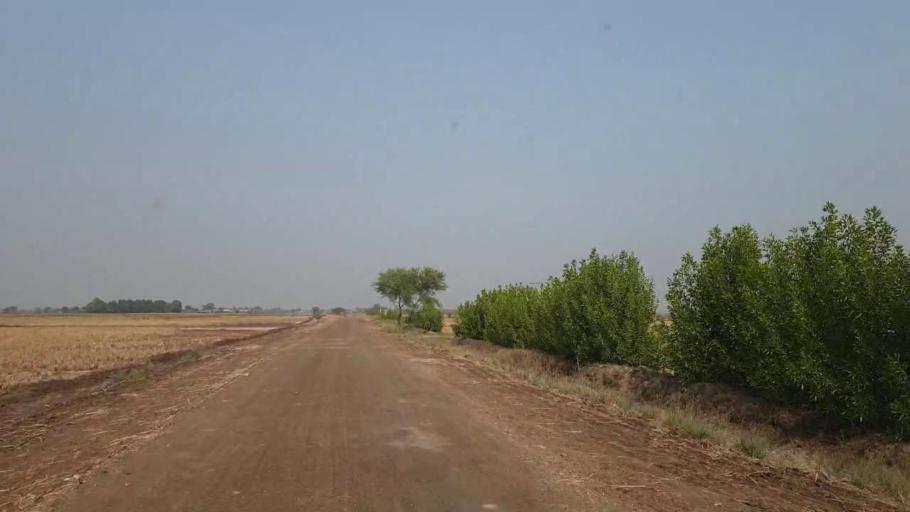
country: PK
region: Sindh
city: Matli
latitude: 25.1499
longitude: 68.7294
